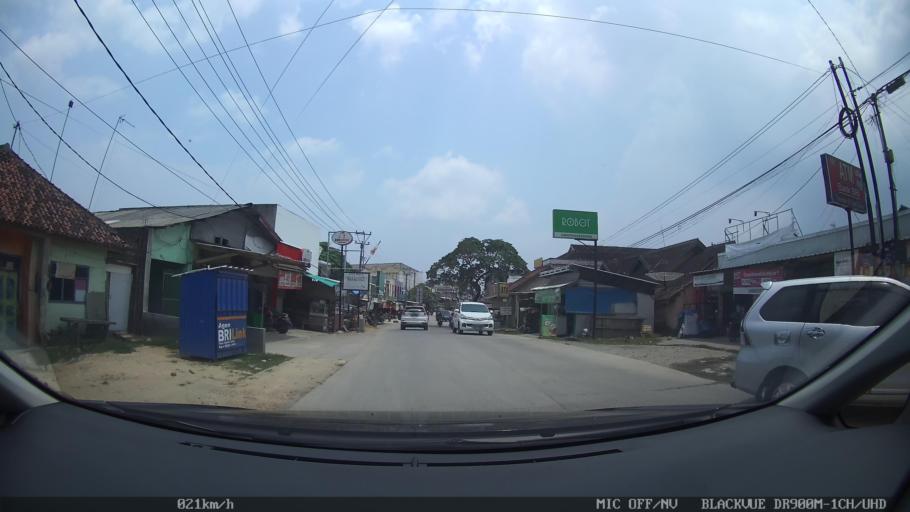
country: ID
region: Lampung
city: Pringsewu
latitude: -5.3539
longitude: 104.9799
